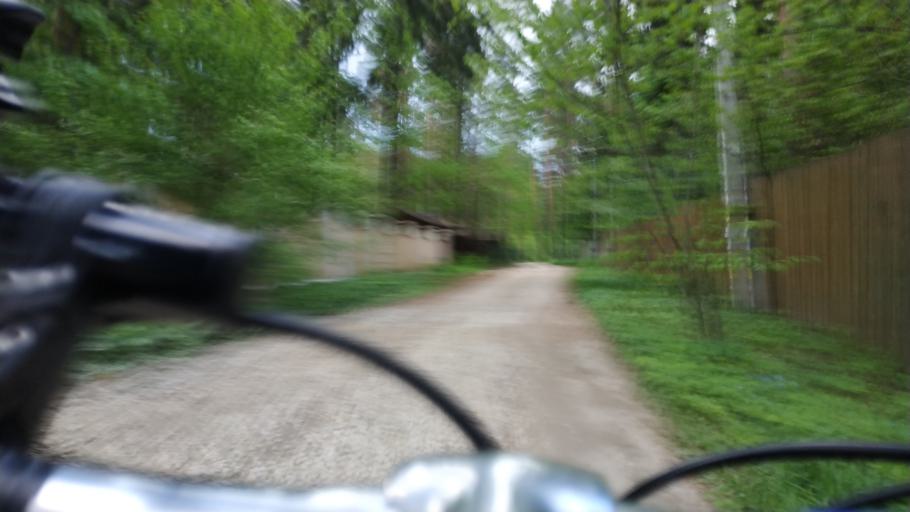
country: RU
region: Moskovskaya
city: Kratovo
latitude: 55.6044
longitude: 38.1563
